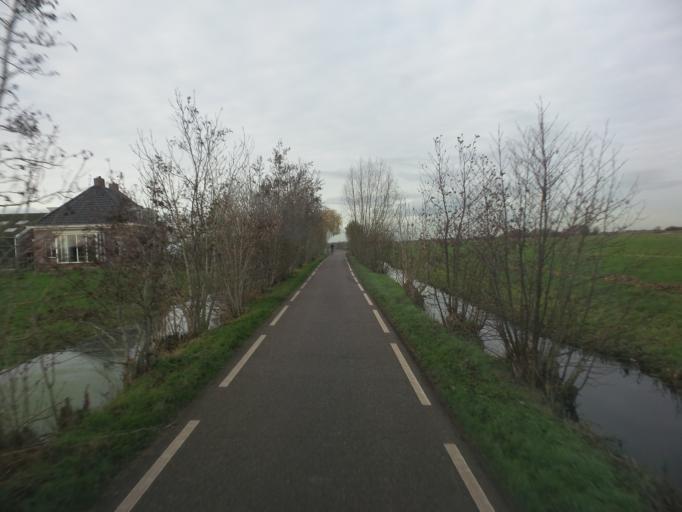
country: NL
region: South Holland
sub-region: Gemeente Vlist
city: Haastrecht
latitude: 52.0223
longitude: 4.7898
